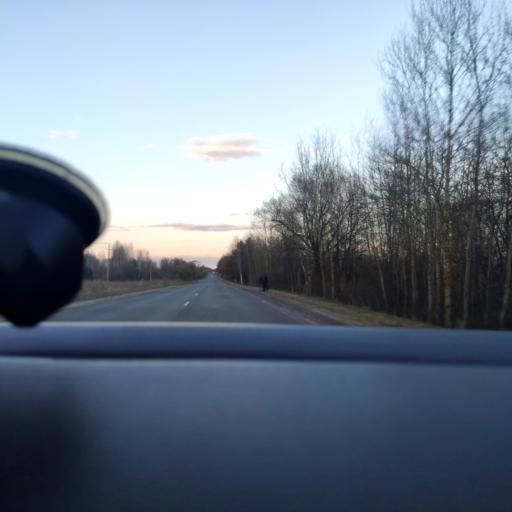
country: RU
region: Moskovskaya
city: Krasnyy Tkach
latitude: 55.4283
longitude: 39.2260
